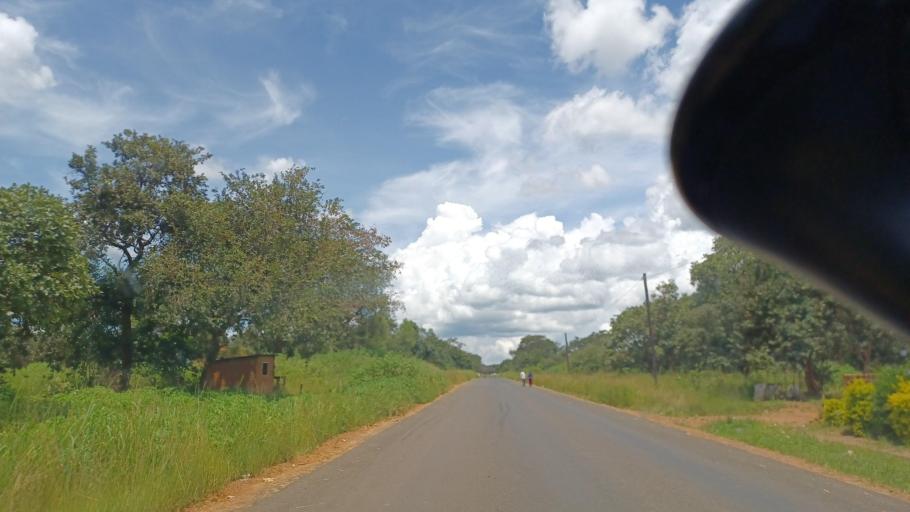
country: ZM
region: North-Western
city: Solwezi
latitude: -12.3982
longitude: 26.2388
